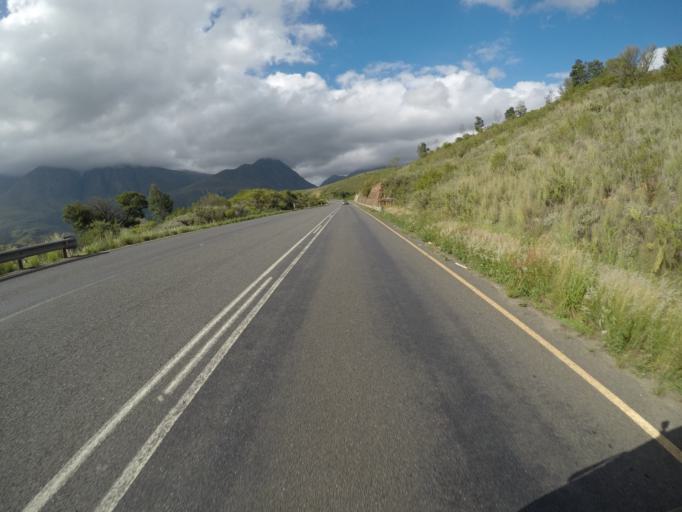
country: ZA
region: Western Cape
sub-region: Overberg District Municipality
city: Swellendam
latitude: -33.9997
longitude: 20.3378
